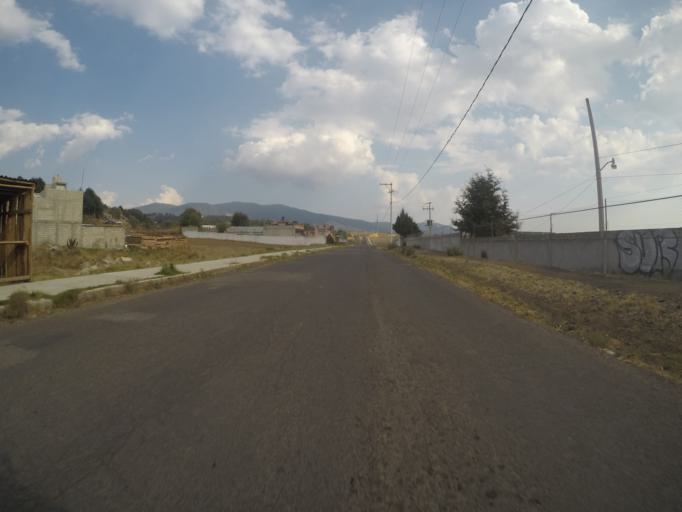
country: MX
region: Mexico
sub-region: Xalatlaco
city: El Aguila (La Mesa)
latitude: 19.1645
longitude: -99.4072
